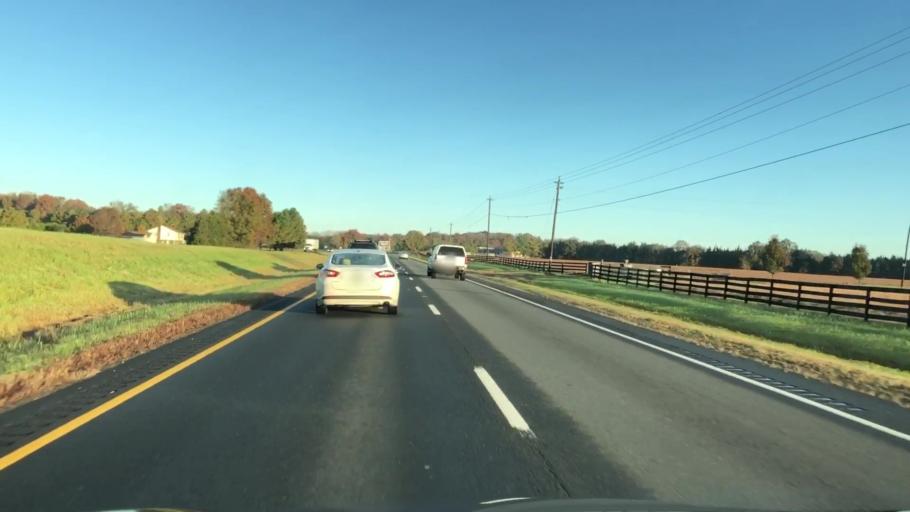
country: US
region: Virginia
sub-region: Fauquier County
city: Bealeton
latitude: 38.5524
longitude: -77.7329
